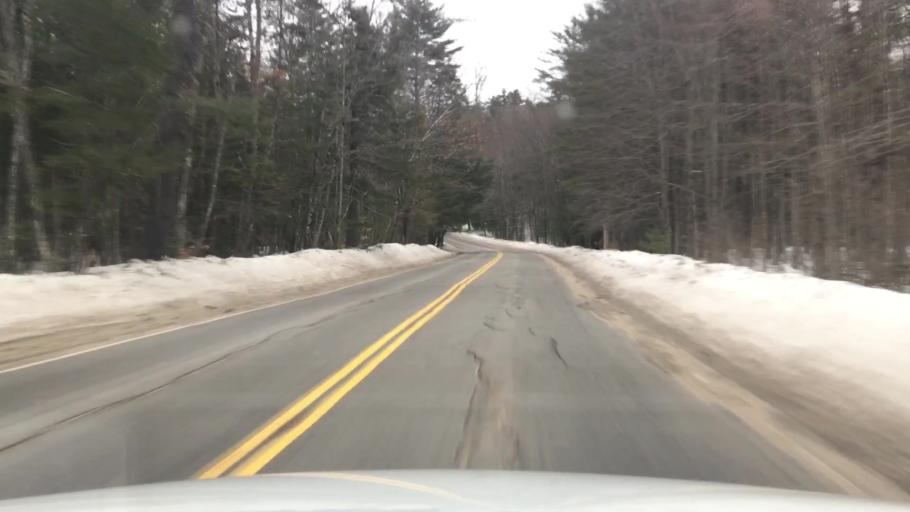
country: US
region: Maine
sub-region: Oxford County
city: Hiram
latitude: 43.8952
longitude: -70.7916
